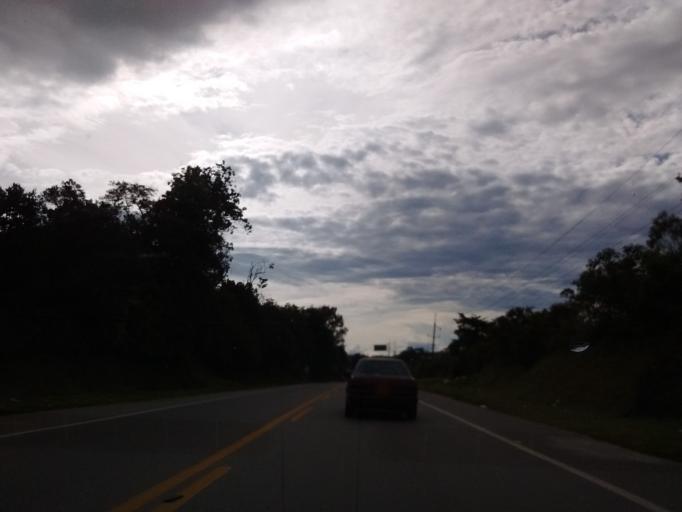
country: CO
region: Antioquia
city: Santuario
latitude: 6.1261
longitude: -75.2496
